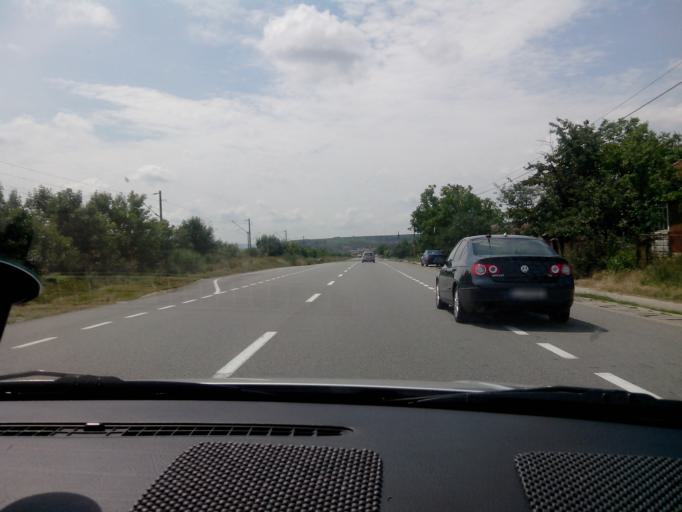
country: RO
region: Cluj
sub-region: Comuna Apahida
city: Apahida
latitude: 46.8450
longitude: 23.7516
